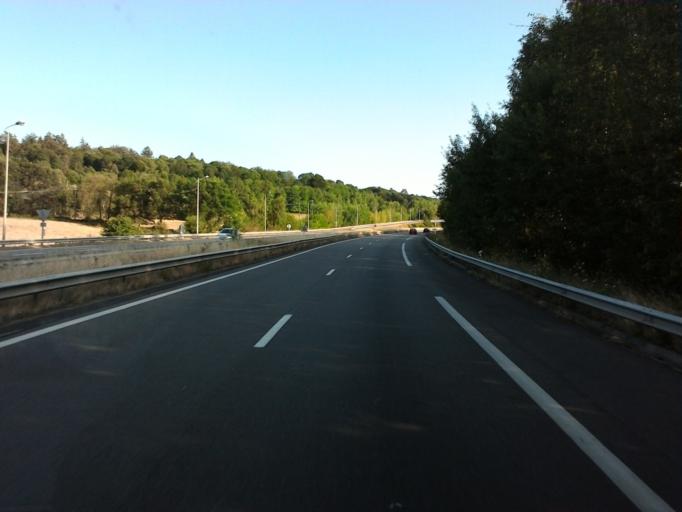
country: FR
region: Lorraine
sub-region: Departement des Vosges
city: Epinal
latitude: 48.1812
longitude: 6.4845
